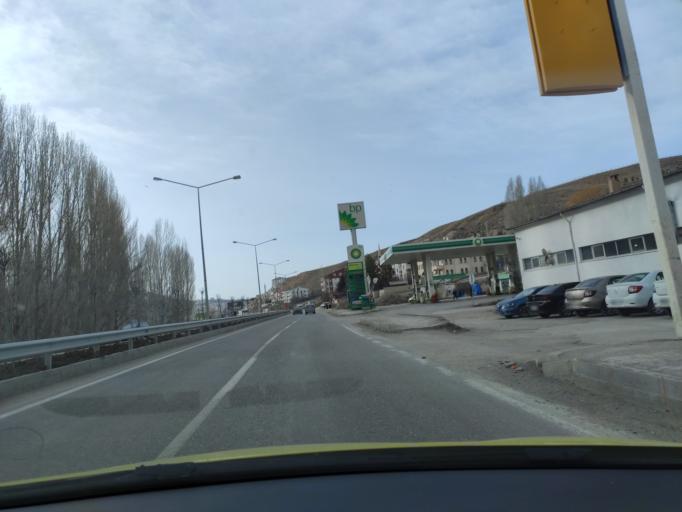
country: TR
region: Bayburt
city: Bayburt
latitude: 40.2419
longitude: 40.2450
